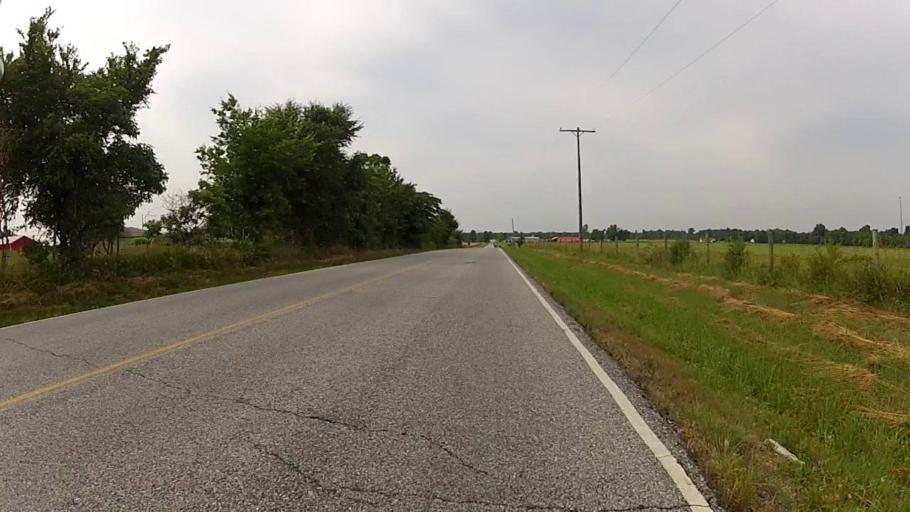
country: US
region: Kansas
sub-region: Cherokee County
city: Baxter Springs
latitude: 37.0793
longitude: -94.7223
